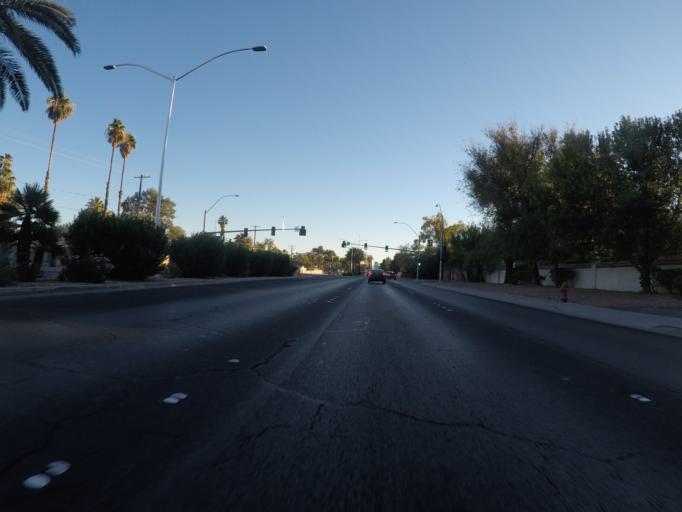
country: US
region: Nevada
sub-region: Clark County
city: Las Vegas
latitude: 36.1686
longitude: -115.1727
